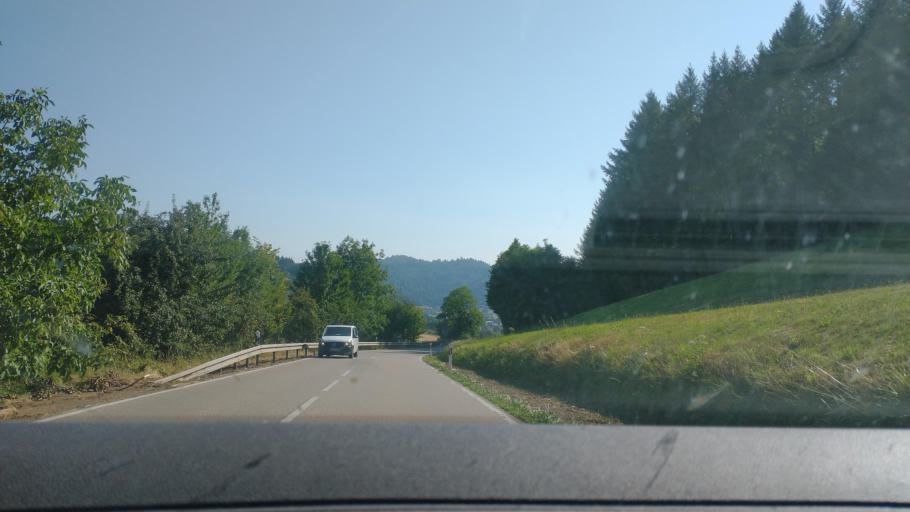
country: DE
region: Baden-Wuerttemberg
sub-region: Freiburg Region
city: Biberach
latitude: 48.3310
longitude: 8.0074
